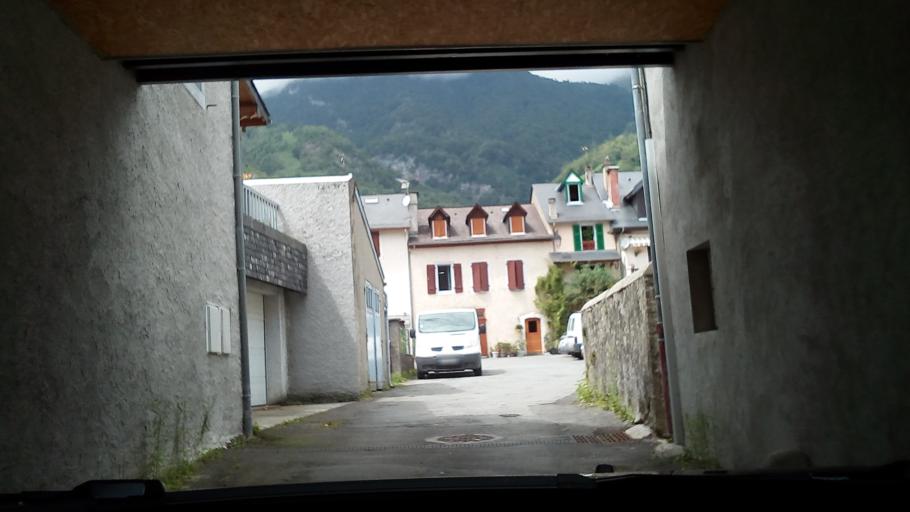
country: FR
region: Aquitaine
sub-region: Departement des Pyrenees-Atlantiques
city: Laruns
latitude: 42.9859
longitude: -0.4272
